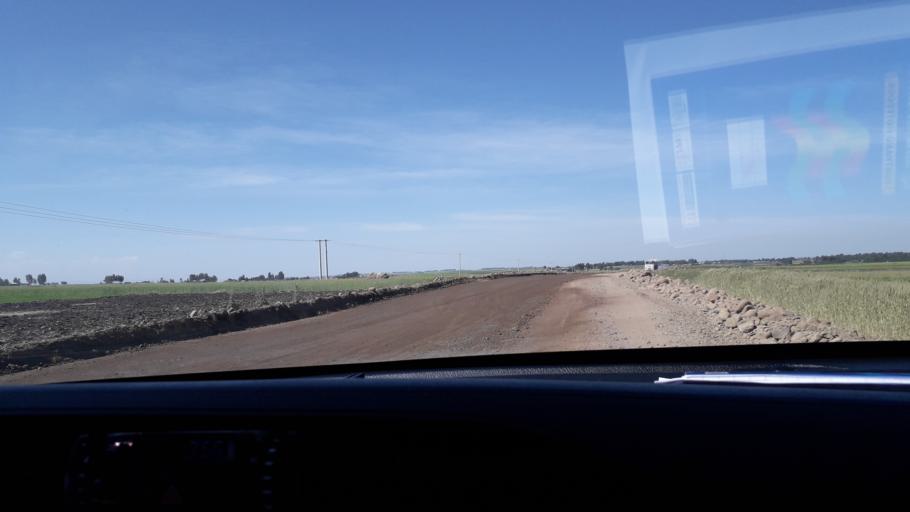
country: ET
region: Amhara
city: Lalibela
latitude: 11.5712
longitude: 39.1678
